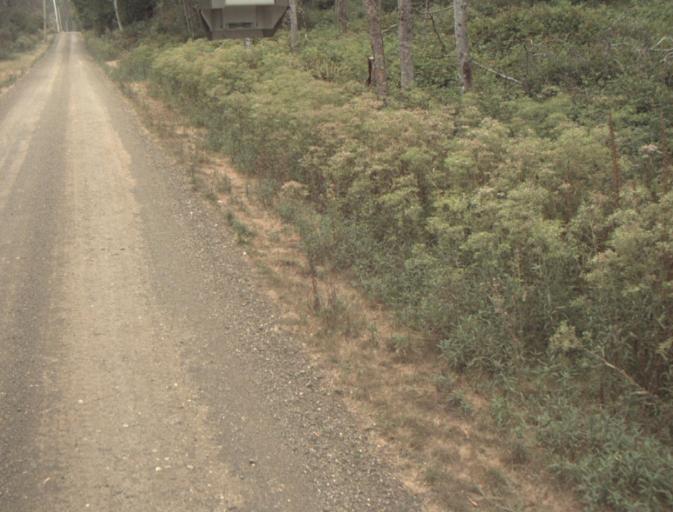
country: AU
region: Tasmania
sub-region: Dorset
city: Bridport
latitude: -41.1944
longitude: 147.2631
